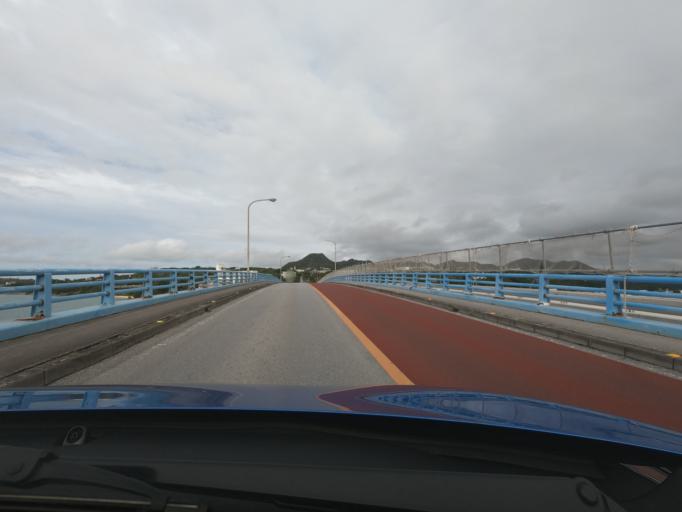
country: JP
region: Okinawa
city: Nago
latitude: 26.6604
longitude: 127.8887
